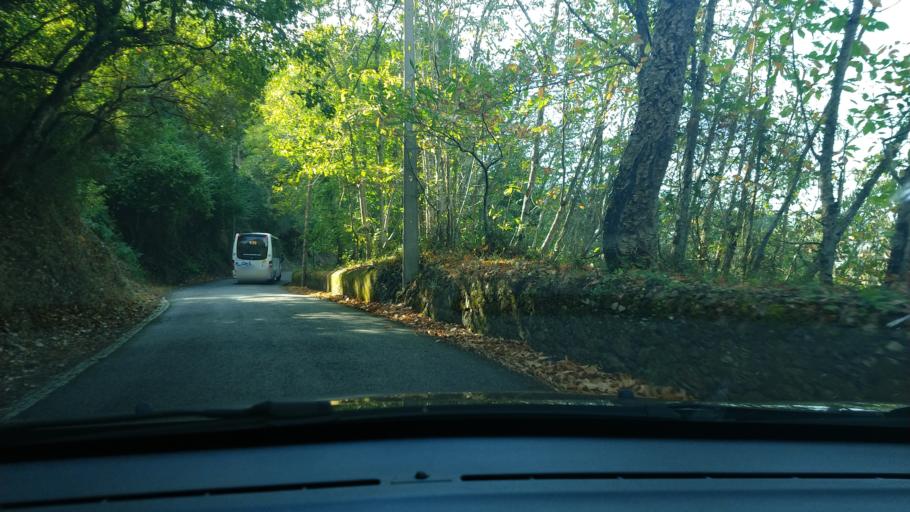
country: PT
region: Lisbon
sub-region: Sintra
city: Colares
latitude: 38.7978
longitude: -9.4398
